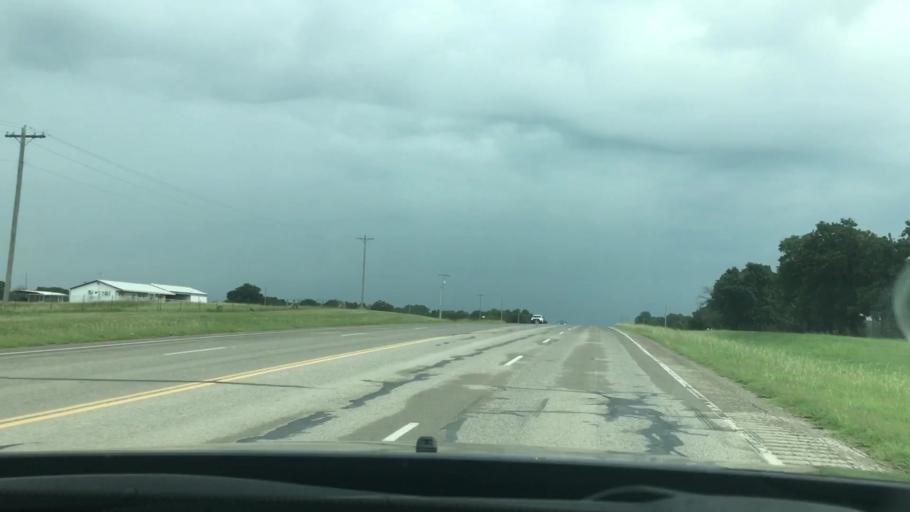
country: US
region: Oklahoma
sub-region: Carter County
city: Healdton
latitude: 34.1913
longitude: -97.4747
